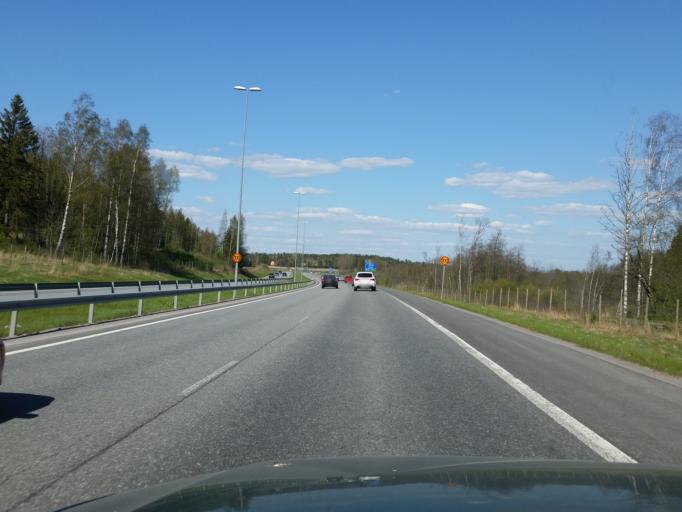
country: FI
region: Uusimaa
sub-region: Helsinki
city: Kirkkonummi
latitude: 60.1238
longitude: 24.4882
